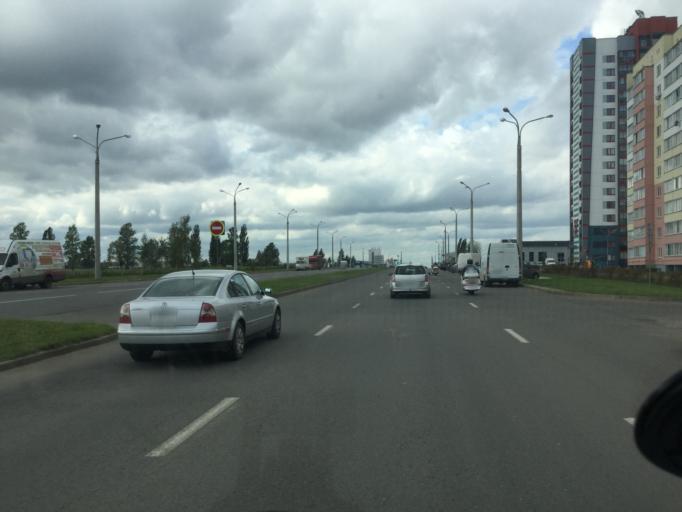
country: BY
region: Vitebsk
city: Vitebsk
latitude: 55.1659
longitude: 30.2600
